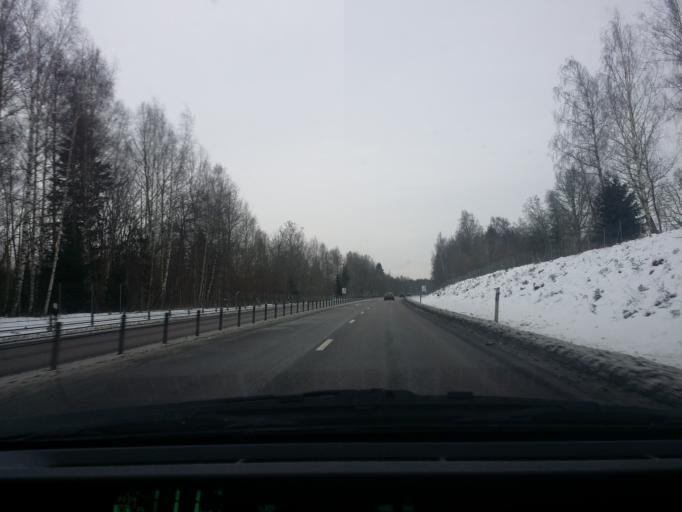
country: SE
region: Vaestra Goetaland
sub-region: Skovde Kommun
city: Stopen
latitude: 58.4891
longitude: 13.8507
